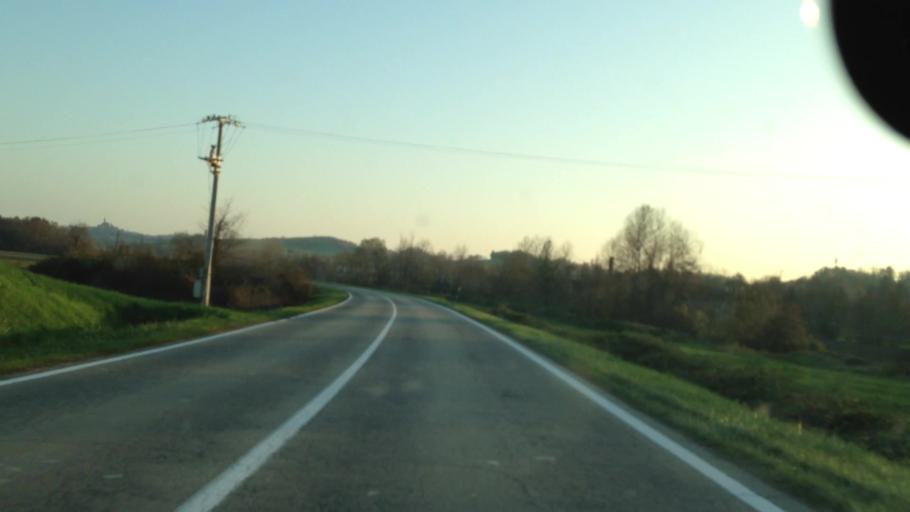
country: IT
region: Piedmont
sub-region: Provincia di Asti
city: Cunico
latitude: 45.0405
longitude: 8.1116
